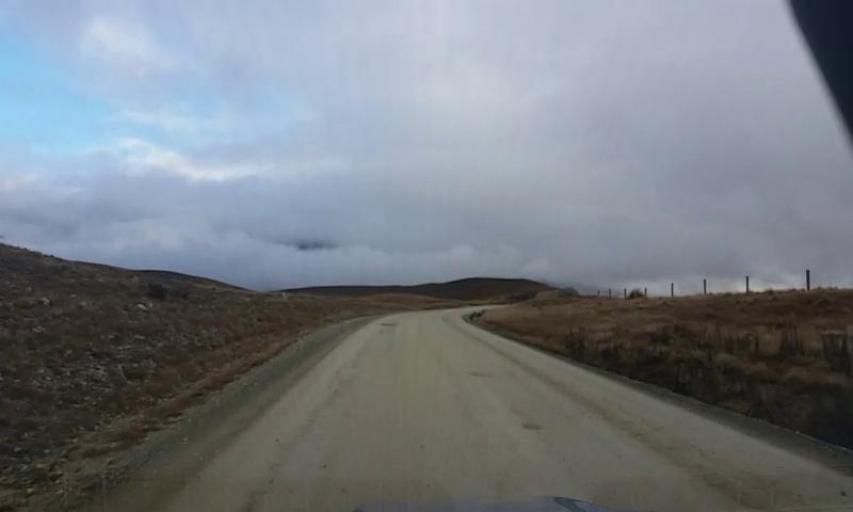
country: NZ
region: Canterbury
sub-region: Ashburton District
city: Methven
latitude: -43.6150
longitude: 171.1462
